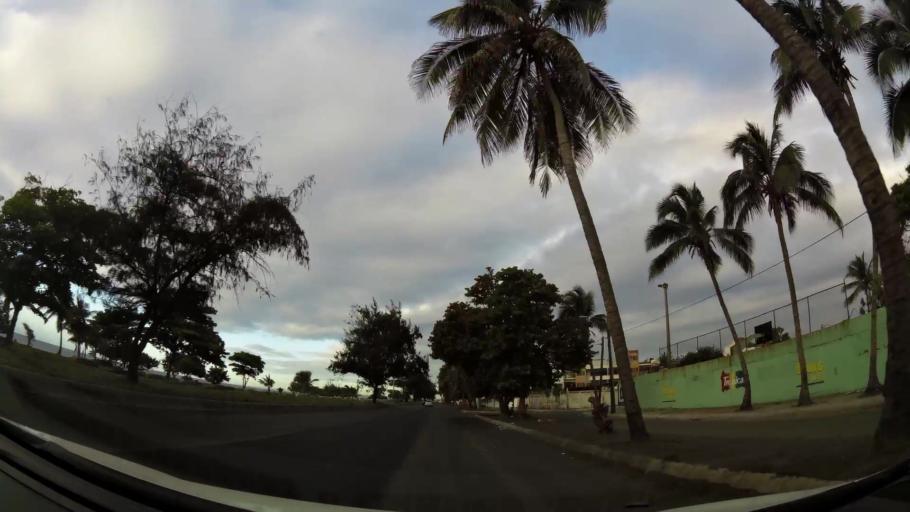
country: DO
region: Nacional
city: Bella Vista
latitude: 18.4294
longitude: -69.9641
